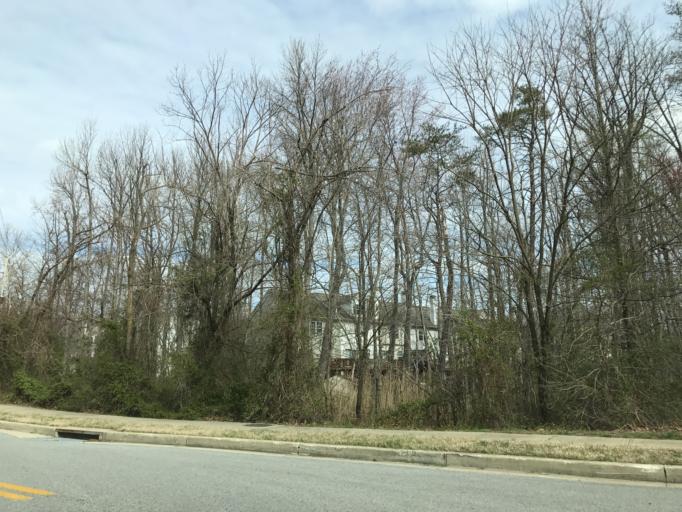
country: US
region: Maryland
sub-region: Baltimore County
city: Bowleys Quarters
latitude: 39.2973
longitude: -76.4126
